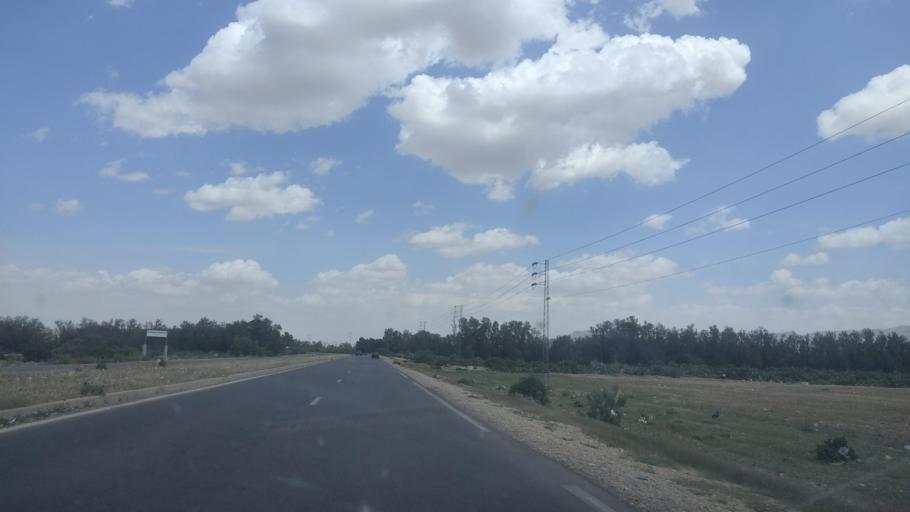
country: TN
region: Al Qasrayn
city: Kasserine
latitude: 35.1983
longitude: 8.8656
